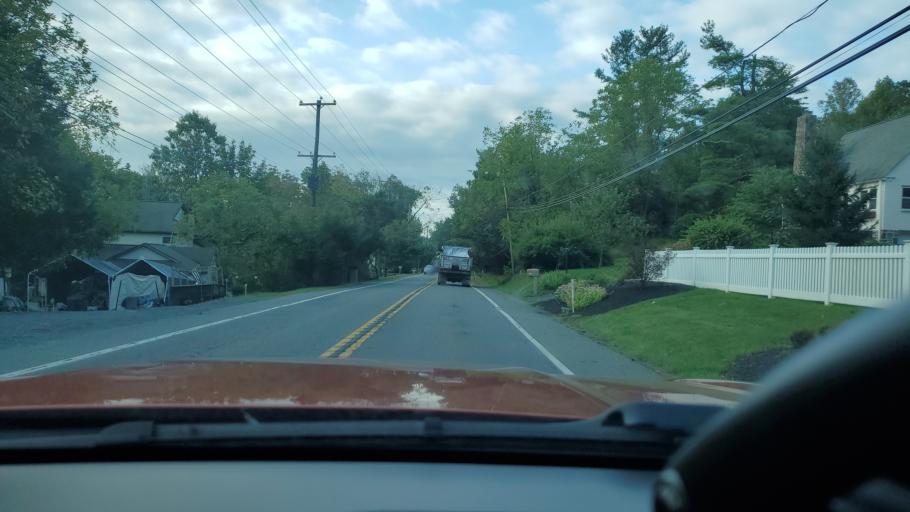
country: US
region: Pennsylvania
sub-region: Montgomery County
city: Woxall
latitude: 40.3098
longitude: -75.4807
